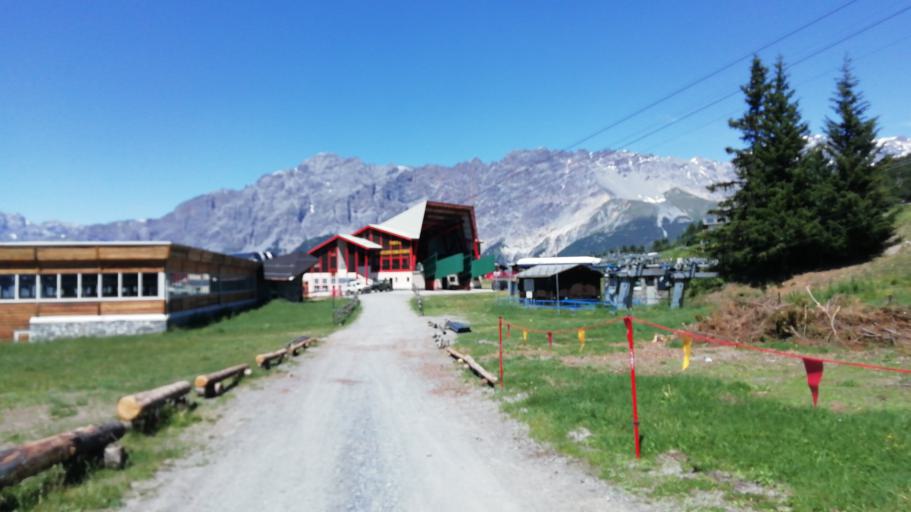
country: IT
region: Lombardy
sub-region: Provincia di Sondrio
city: San Nicolo
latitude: 46.4429
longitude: 10.3882
